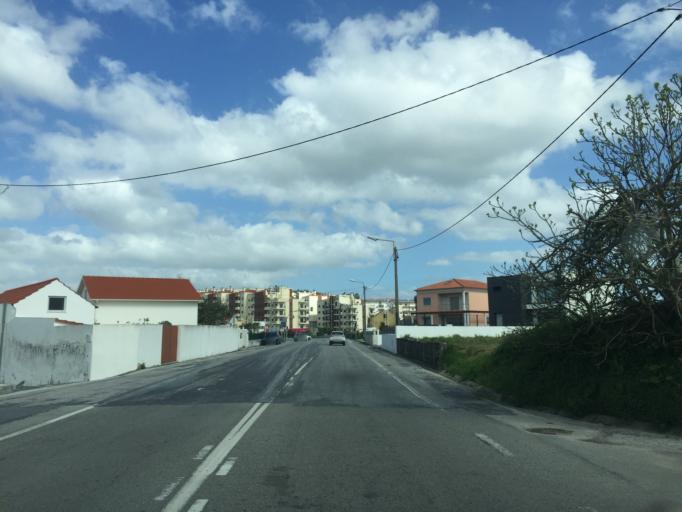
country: PT
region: Coimbra
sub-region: Figueira da Foz
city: Tavarede
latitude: 40.1635
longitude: -8.8388
